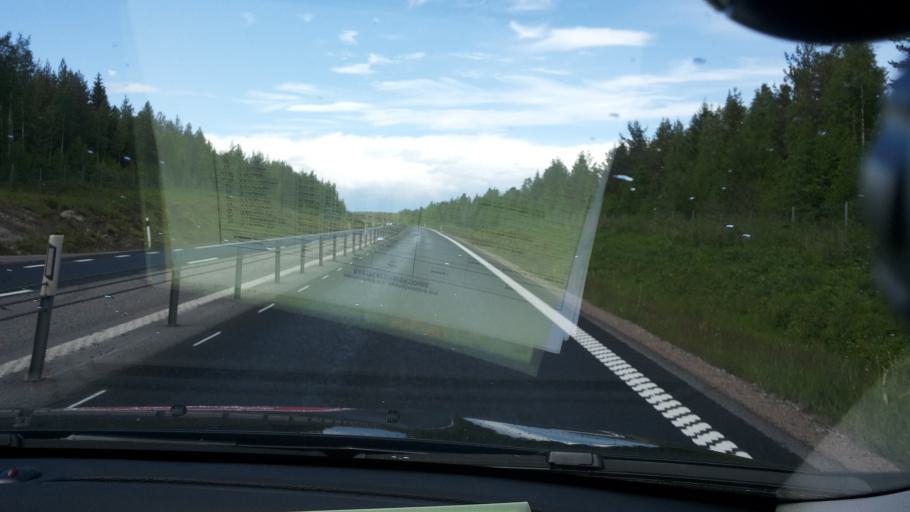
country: SE
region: Vaesternorrland
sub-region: Sundsvalls Kommun
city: Njurundabommen
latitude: 62.1750
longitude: 17.3570
